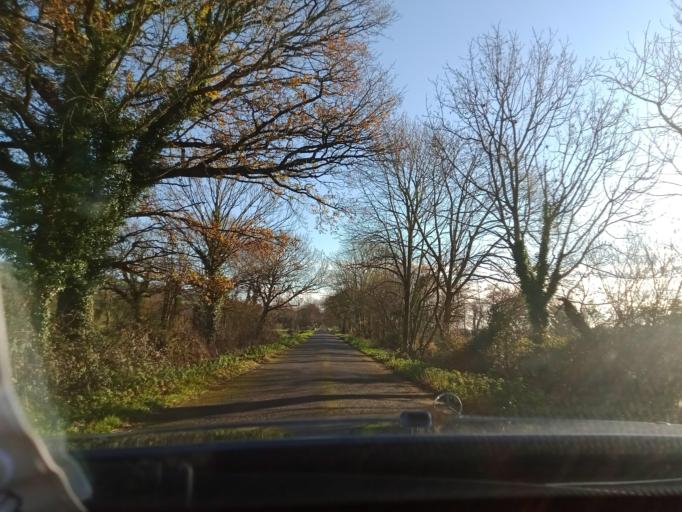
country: IE
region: Leinster
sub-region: Kilkenny
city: Piltown
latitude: 52.3528
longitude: -7.2910
